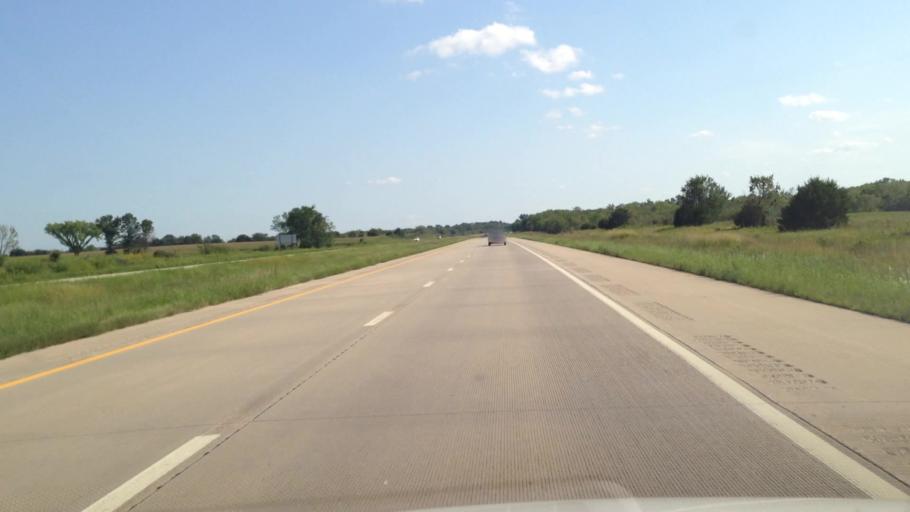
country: US
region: Kansas
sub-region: Bourbon County
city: Fort Scott
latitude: 37.9178
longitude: -94.7044
